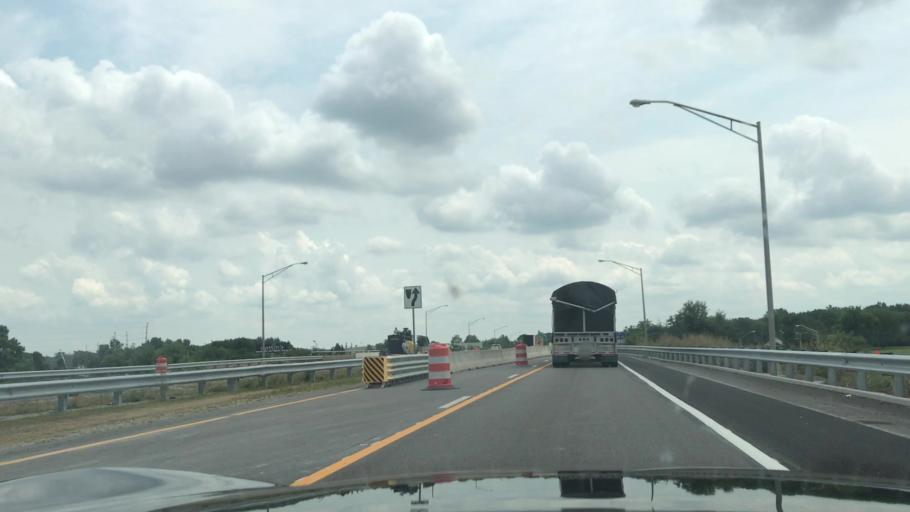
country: US
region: Kentucky
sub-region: Warren County
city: Bowling Green
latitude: 36.9584
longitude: -86.4974
